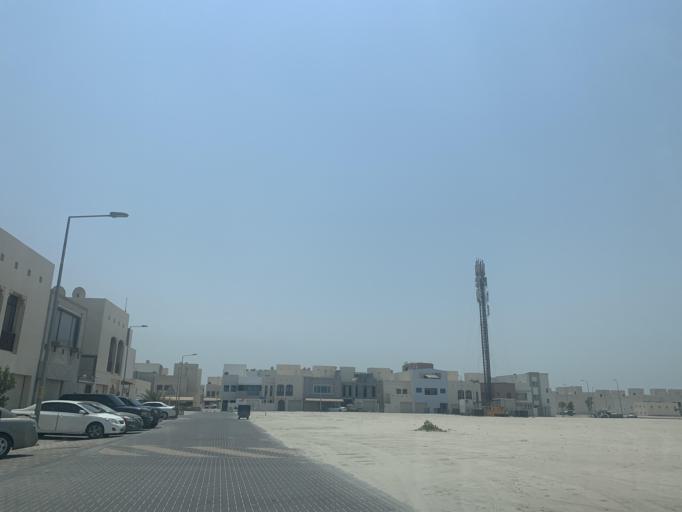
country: BH
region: Muharraq
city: Al Hadd
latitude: 26.2366
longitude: 50.6708
